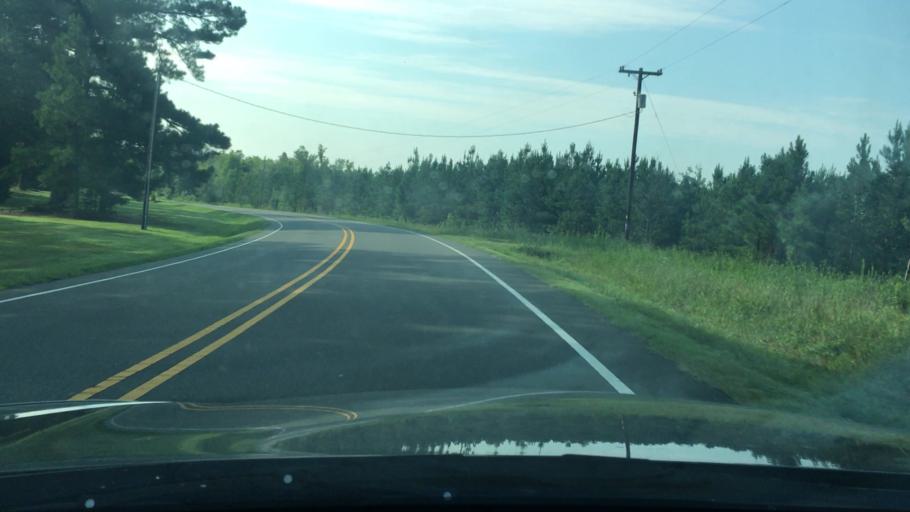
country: US
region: North Carolina
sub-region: Alamance County
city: Green Level
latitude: 36.2584
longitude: -79.3370
